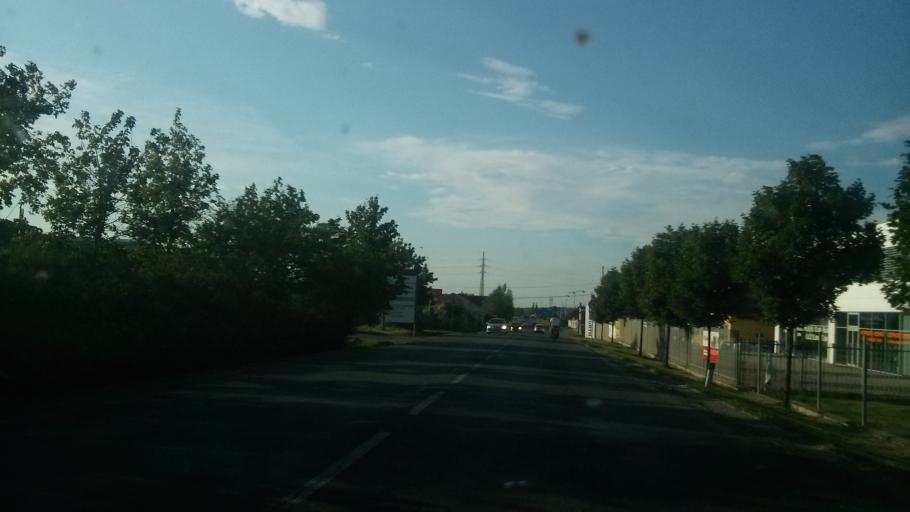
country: CZ
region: Central Bohemia
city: Vestec
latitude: 49.9869
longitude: 14.4933
